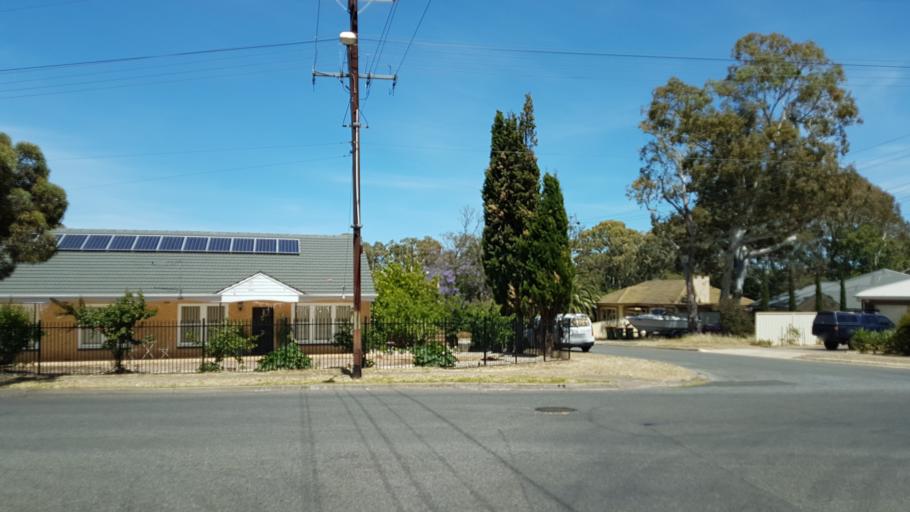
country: AU
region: South Australia
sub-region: Tea Tree Gully
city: Hope Valley
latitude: -34.8228
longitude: 138.7153
